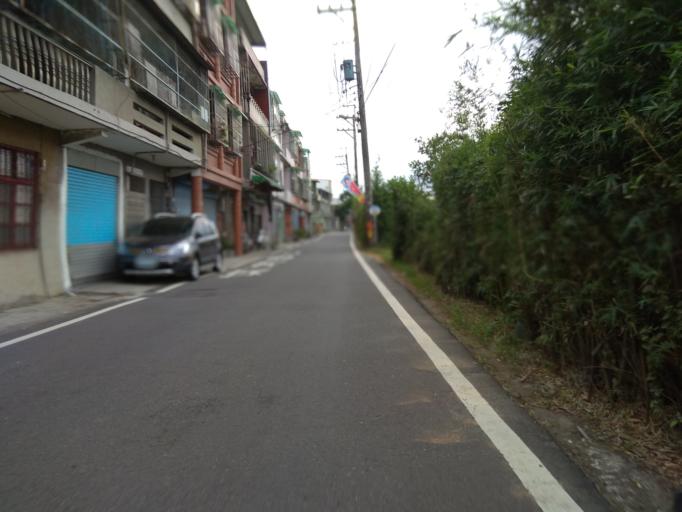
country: TW
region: Taiwan
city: Daxi
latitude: 24.9327
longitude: 121.2049
